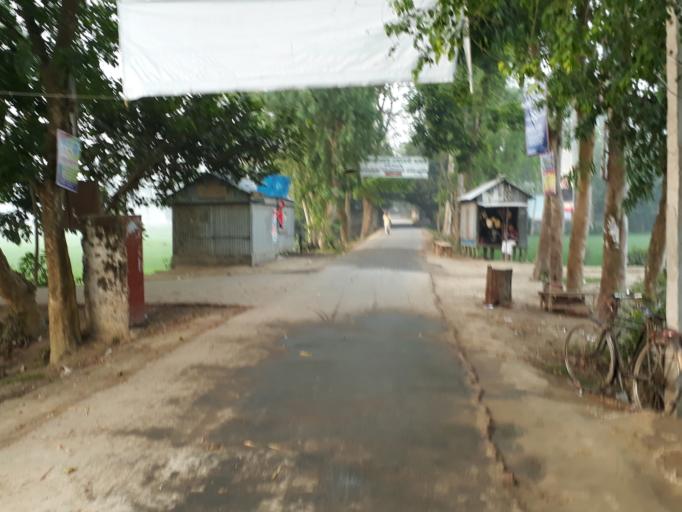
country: BD
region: Rajshahi
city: Sirajganj
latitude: 24.3225
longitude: 89.6744
